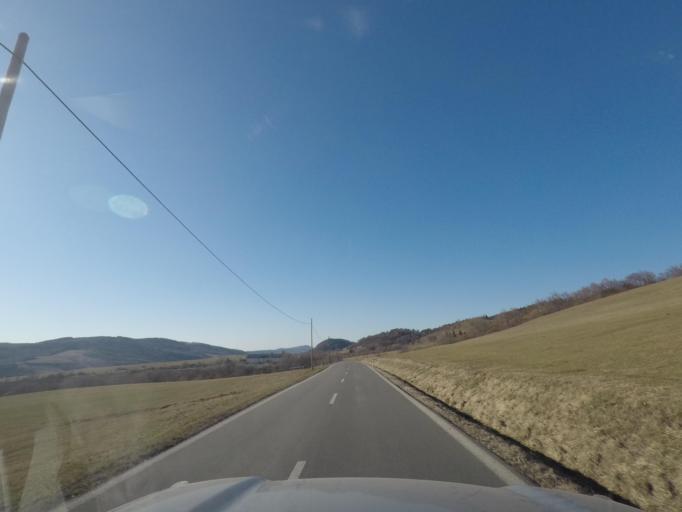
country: SK
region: Presovsky
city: Medzilaborce
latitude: 49.2175
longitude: 21.9820
